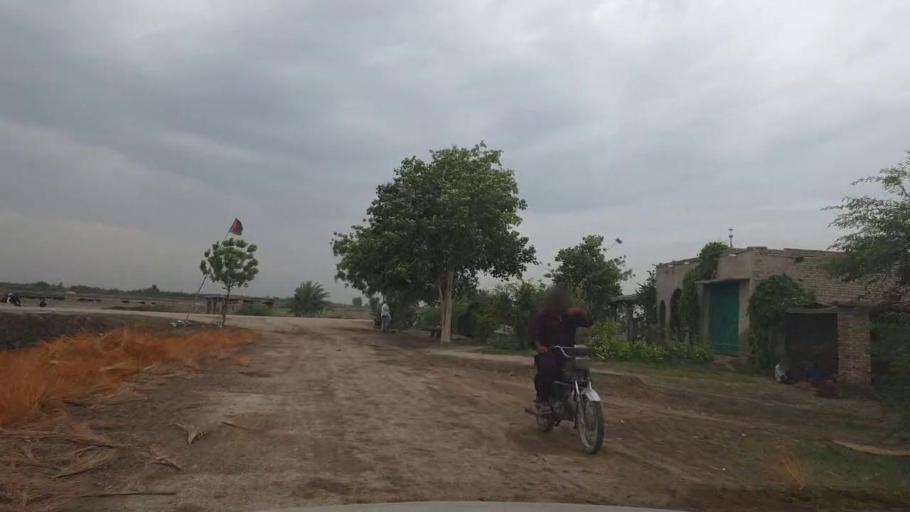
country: PK
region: Sindh
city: Khairpur
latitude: 27.5896
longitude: 68.8130
